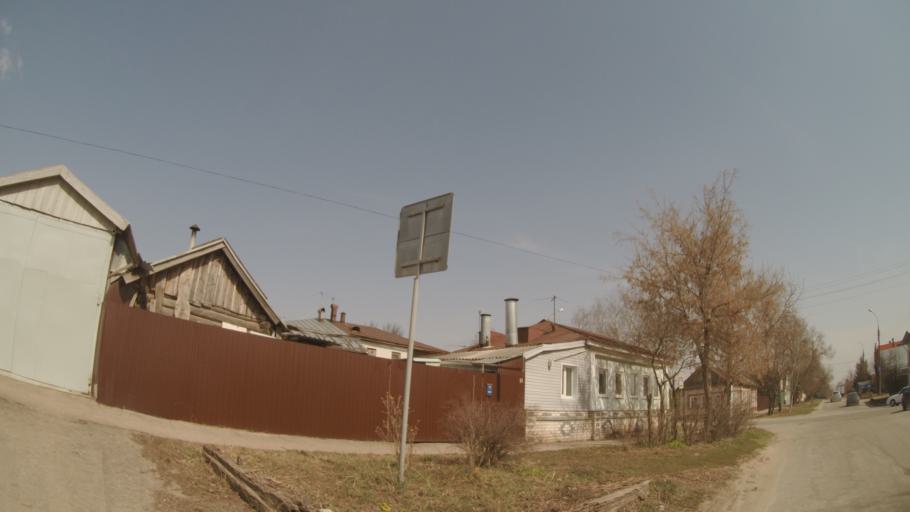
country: RU
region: Nizjnij Novgorod
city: Arzamas
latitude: 55.3850
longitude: 43.8222
